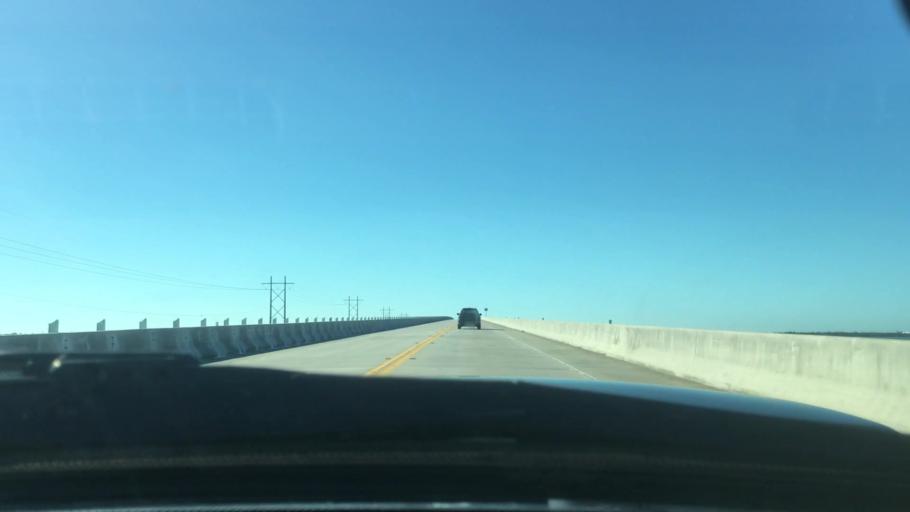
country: US
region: Florida
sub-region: Monroe County
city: Big Pine Key
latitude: 24.6602
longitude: -81.4238
